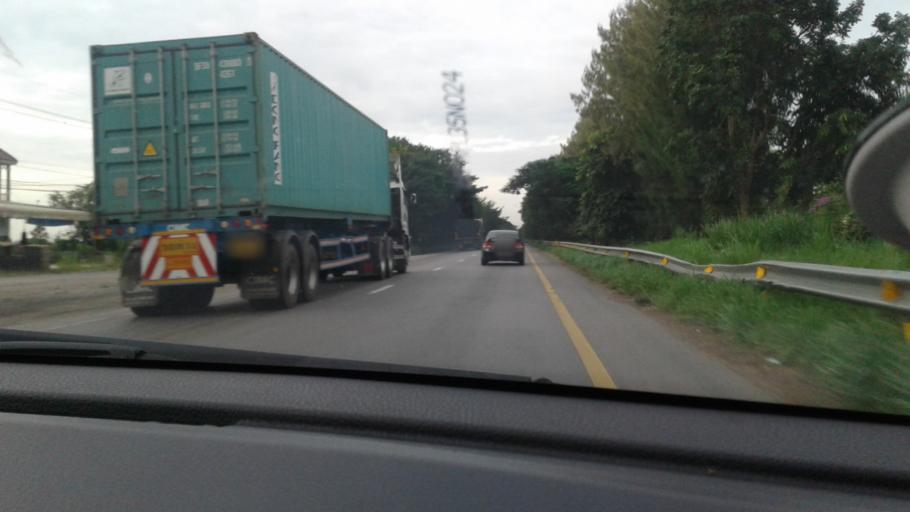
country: TH
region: Prachuap Khiri Khan
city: Pran Buri
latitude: 12.4875
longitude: 99.8906
